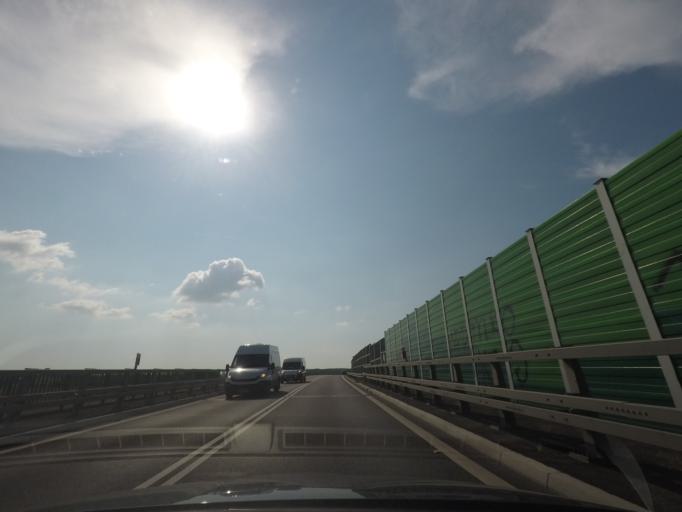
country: PL
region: Silesian Voivodeship
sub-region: Powiat pszczynski
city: Czarkow
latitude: 50.0013
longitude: 18.9210
